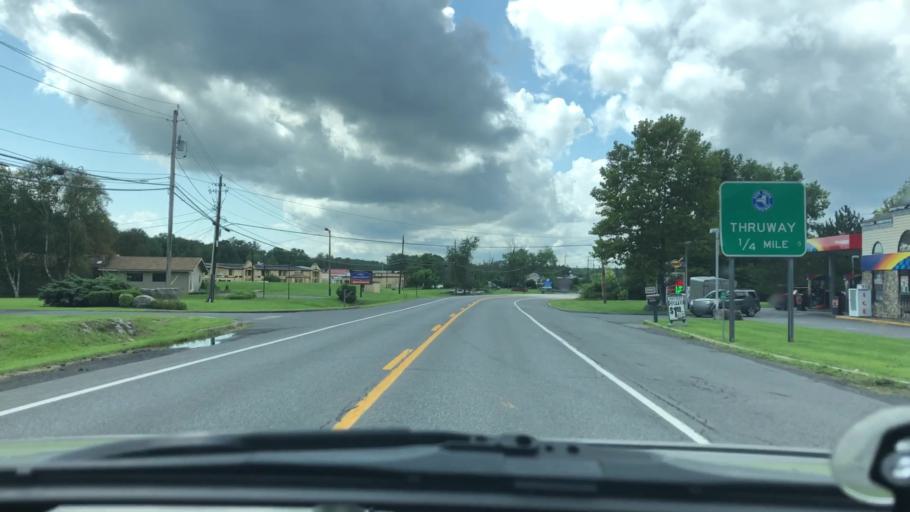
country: US
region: New York
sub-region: Ulster County
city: Saugerties
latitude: 42.0894
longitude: -73.9735
